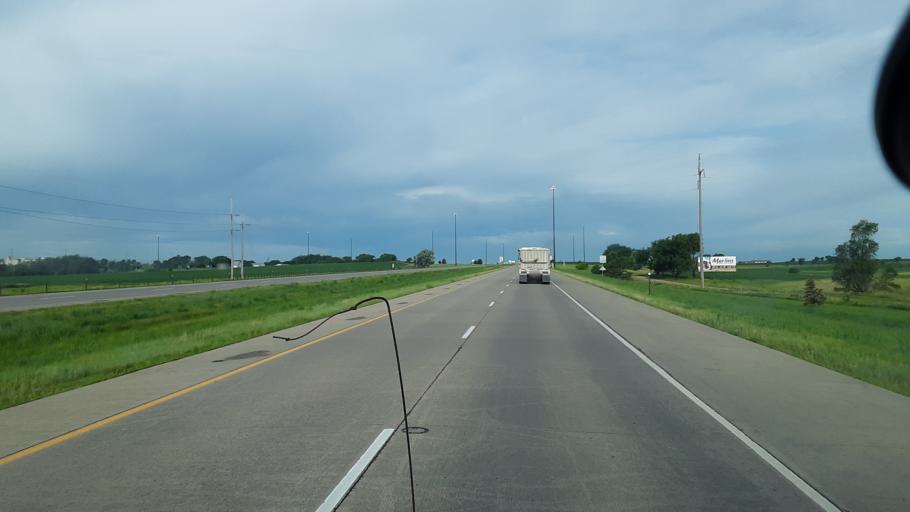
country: US
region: South Dakota
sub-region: Minnehaha County
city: Sioux Falls
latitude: 43.6078
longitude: -96.6795
